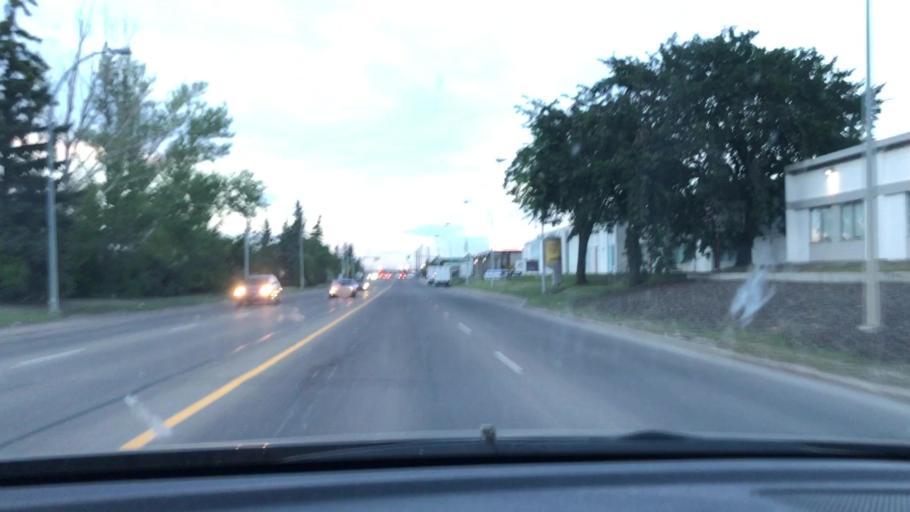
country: CA
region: Alberta
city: Edmonton
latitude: 53.5053
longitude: -113.4490
